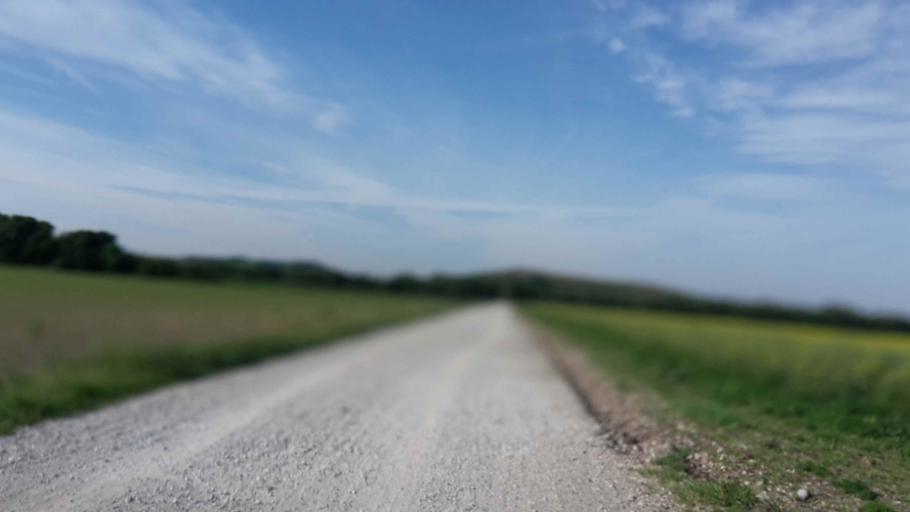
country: DE
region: Bavaria
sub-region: Upper Bavaria
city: Garching bei Munchen
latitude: 48.2354
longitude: 11.6332
